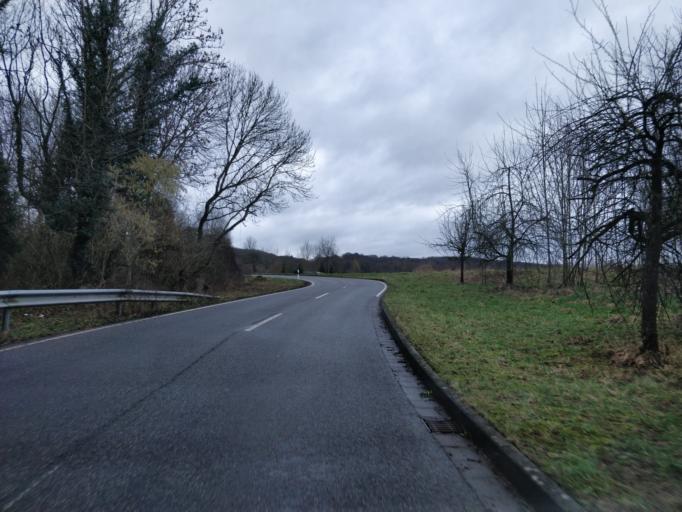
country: DE
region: Rheinland-Pfalz
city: Andernach
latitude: 50.4545
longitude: 7.4126
